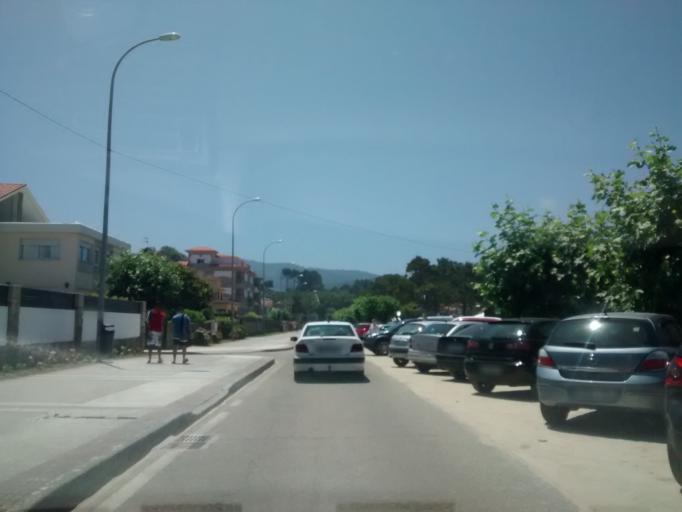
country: ES
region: Galicia
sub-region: Provincia de Pontevedra
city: Nigran
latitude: 42.1281
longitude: -8.8190
